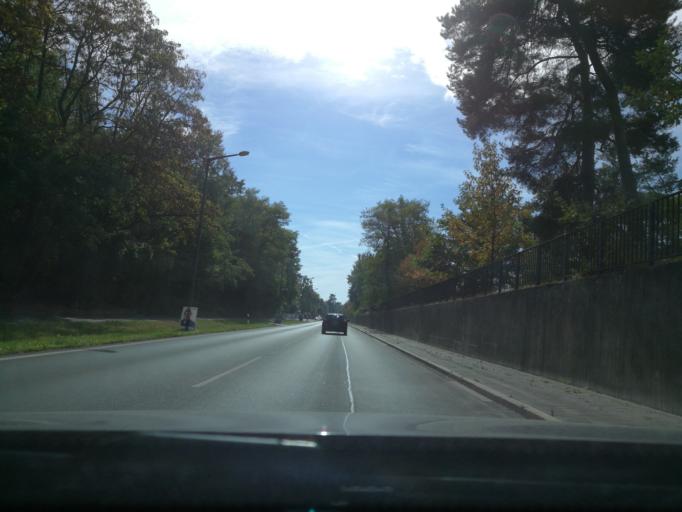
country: DE
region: Bavaria
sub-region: Regierungsbezirk Mittelfranken
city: Furth
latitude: 49.5048
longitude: 10.9668
